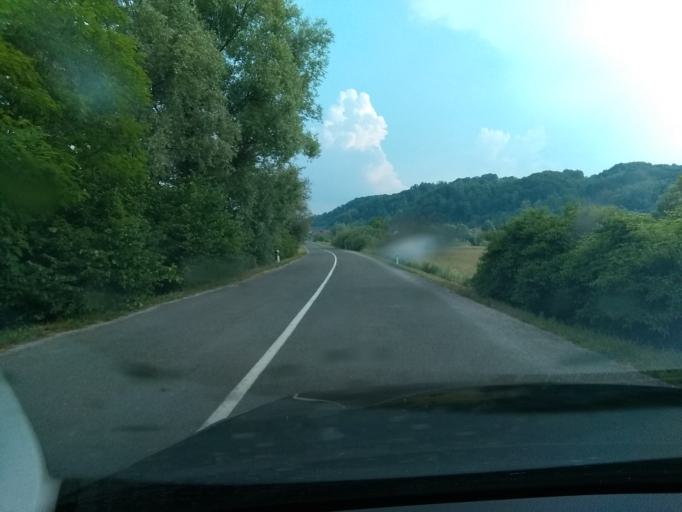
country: HR
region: Krapinsko-Zagorska
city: Pregrada
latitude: 46.0655
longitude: 15.7940
